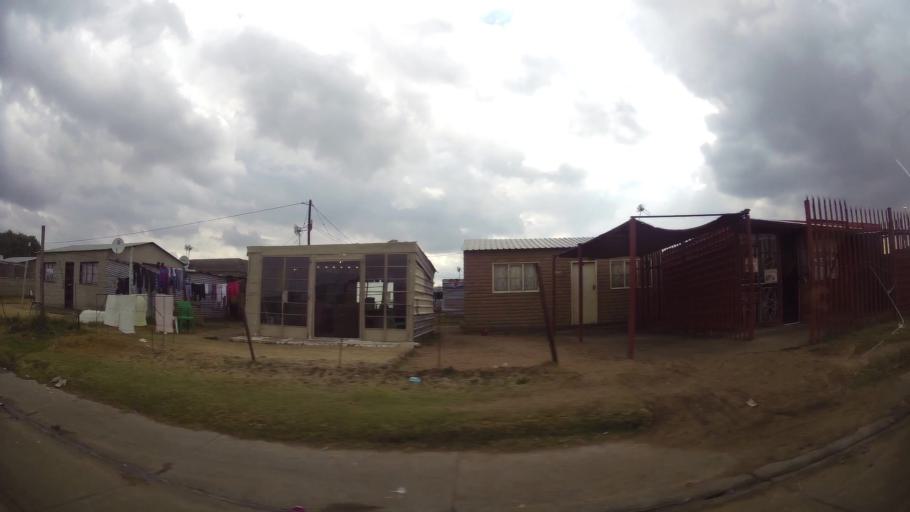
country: ZA
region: Orange Free State
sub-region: Fezile Dabi District Municipality
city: Sasolburg
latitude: -26.8540
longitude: 27.8767
